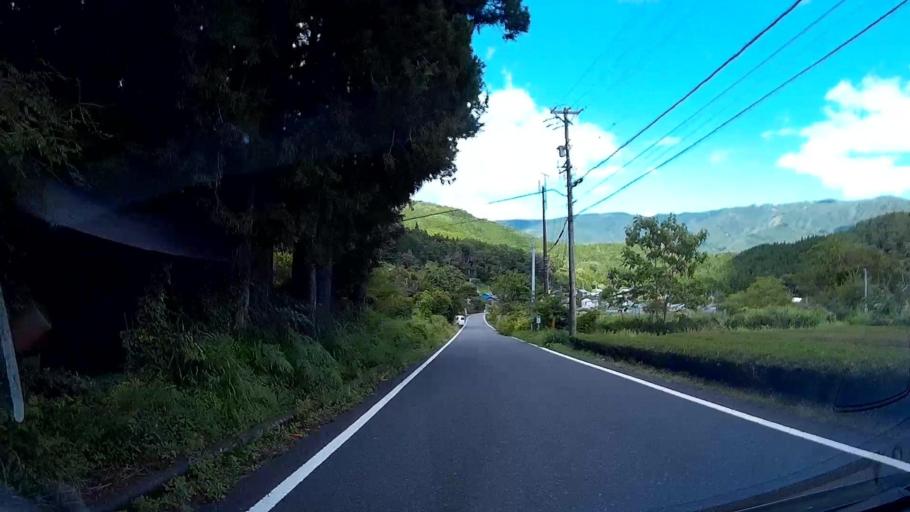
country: JP
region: Shizuoka
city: Shizuoka-shi
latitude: 35.2176
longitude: 138.2239
